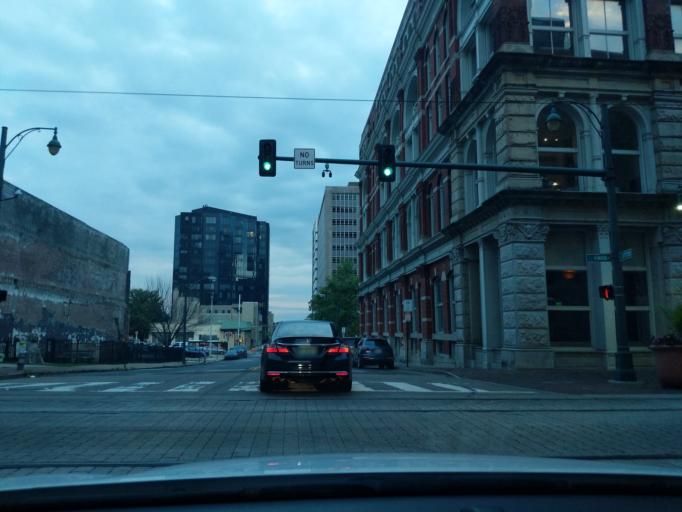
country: US
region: Tennessee
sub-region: Shelby County
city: Memphis
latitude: 35.1472
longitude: -90.0522
